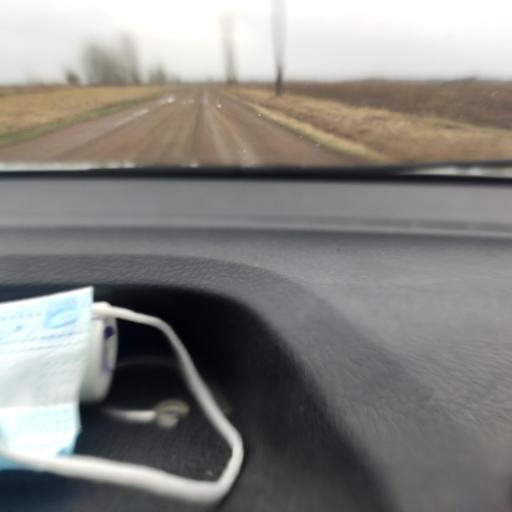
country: RU
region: Bashkortostan
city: Ulukulevo
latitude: 54.4094
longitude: 56.4418
